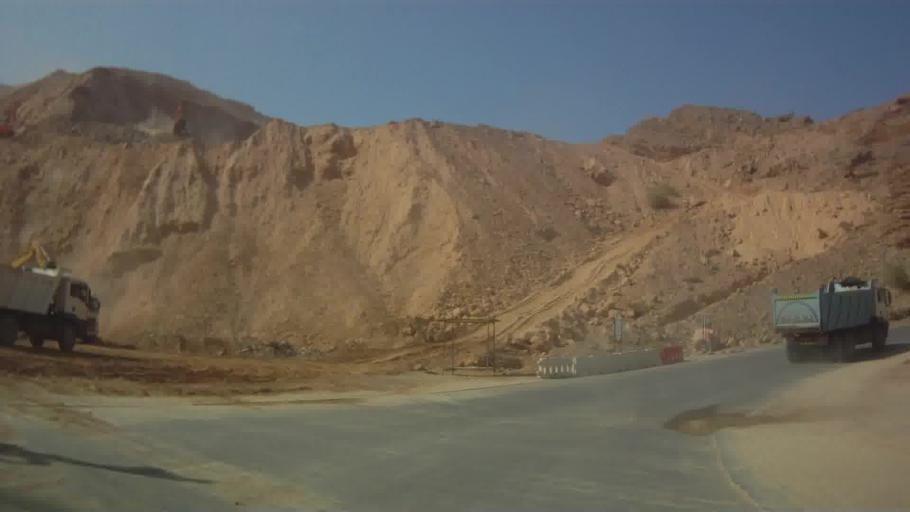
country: OM
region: Muhafazat Masqat
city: Muscat
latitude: 23.5107
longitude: 58.7232
